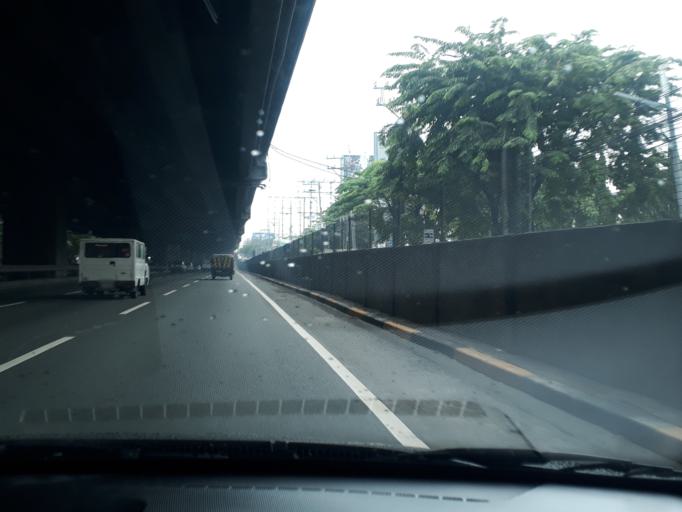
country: PH
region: Calabarzon
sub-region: Province of Rizal
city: Taguig
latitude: 14.5025
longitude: 121.0372
